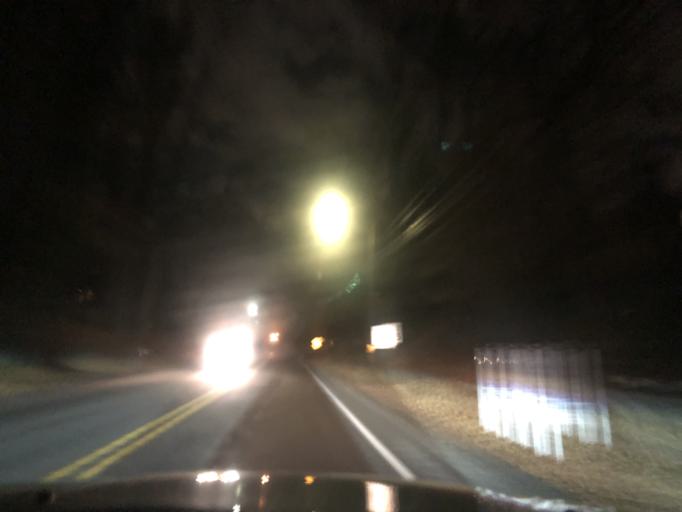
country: US
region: Pennsylvania
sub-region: Delaware County
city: Radnor
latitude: 40.0287
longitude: -75.3582
